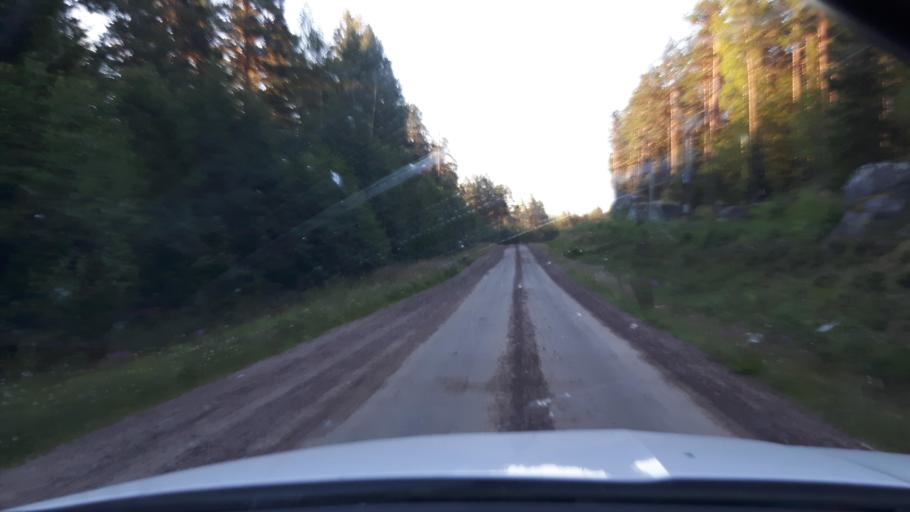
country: SE
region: Vaesternorrland
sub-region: Ange Kommun
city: Ange
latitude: 62.1675
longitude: 15.6523
